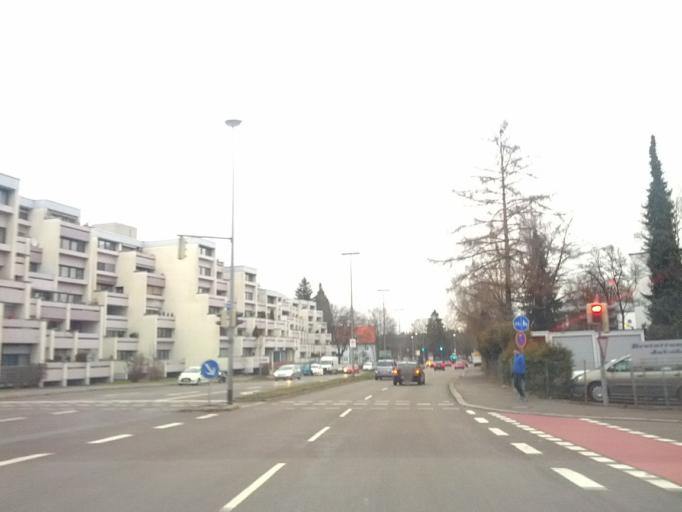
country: DE
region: Bavaria
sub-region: Swabia
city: Kempten (Allgaeu)
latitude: 47.7342
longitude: 10.3064
